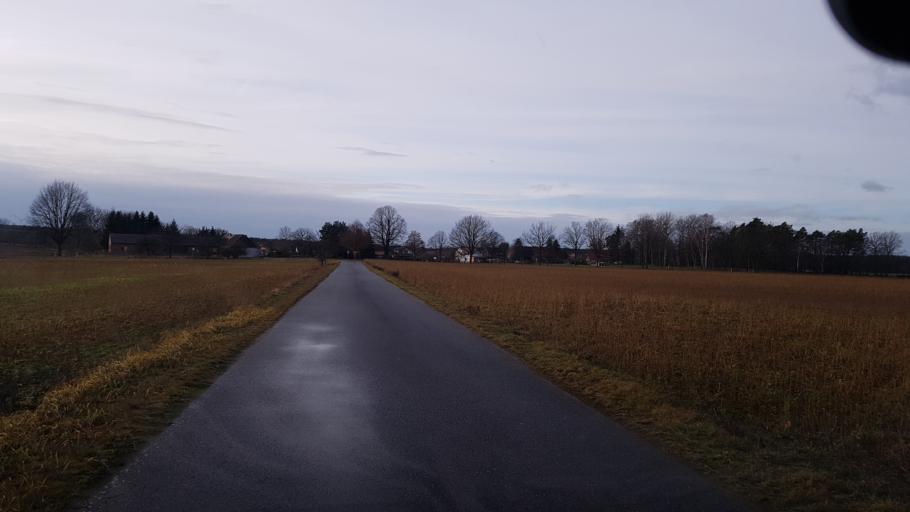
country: DE
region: Brandenburg
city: Bronkow
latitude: 51.6663
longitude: 13.8675
